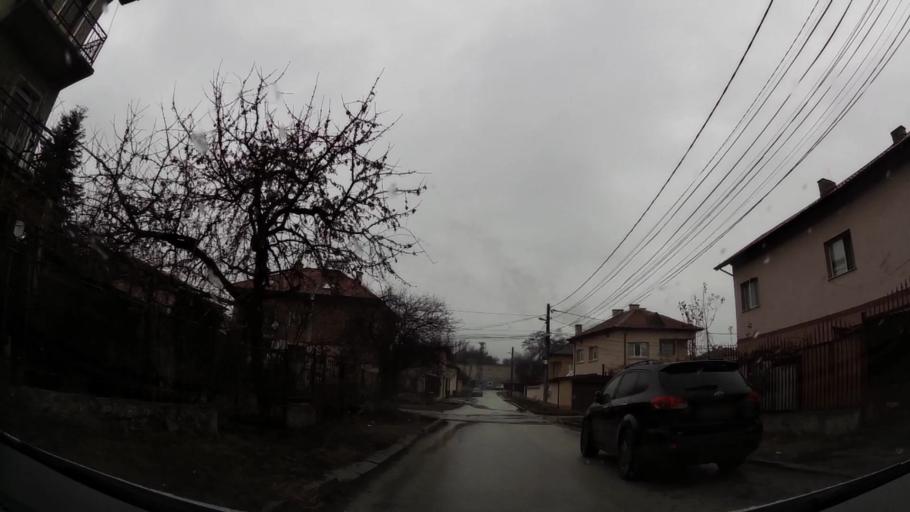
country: BG
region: Sofia-Capital
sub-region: Stolichna Obshtina
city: Sofia
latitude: 42.6247
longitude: 23.4020
